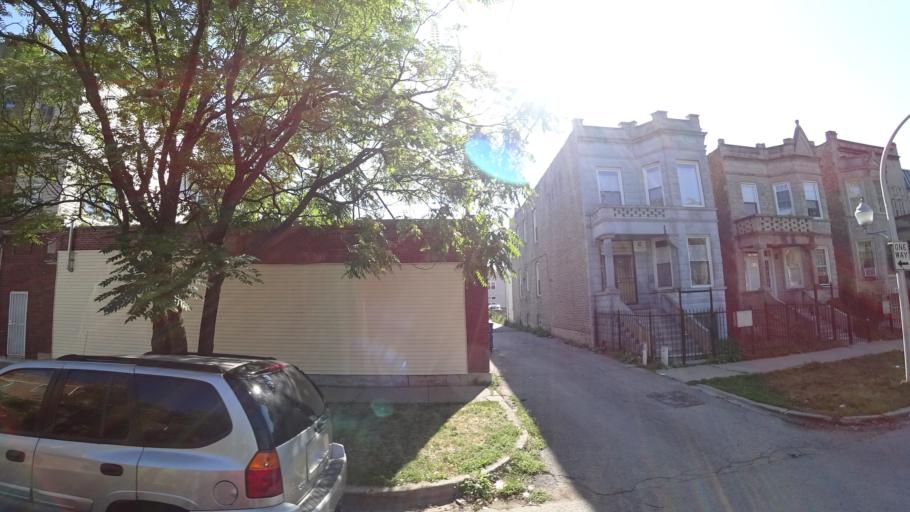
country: US
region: Illinois
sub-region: Cook County
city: Cicero
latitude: 41.8658
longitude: -87.7239
